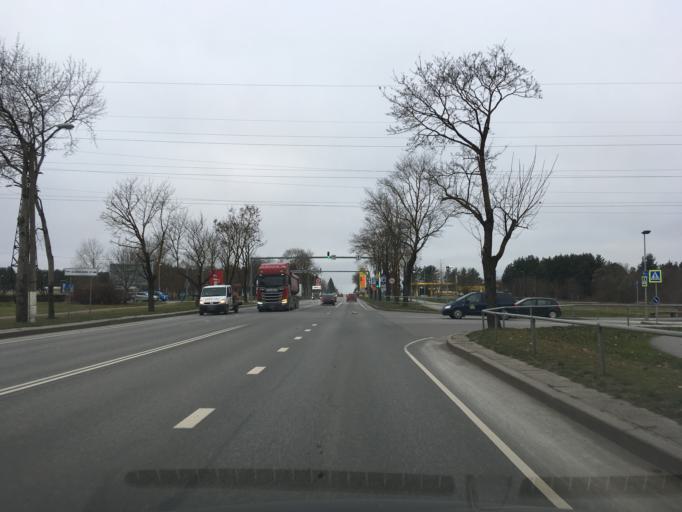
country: EE
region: Ida-Virumaa
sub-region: Narva linn
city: Narva
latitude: 59.3837
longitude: 28.1615
